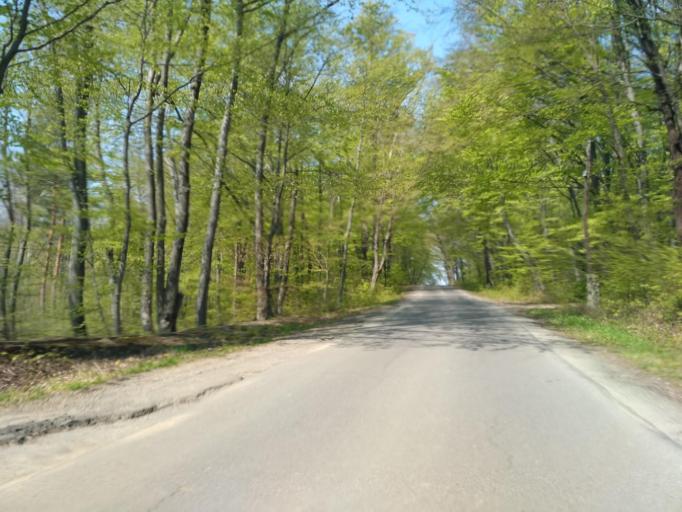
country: PL
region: Subcarpathian Voivodeship
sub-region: Powiat krosnienski
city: Chorkowka
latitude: 49.6150
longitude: 21.7140
